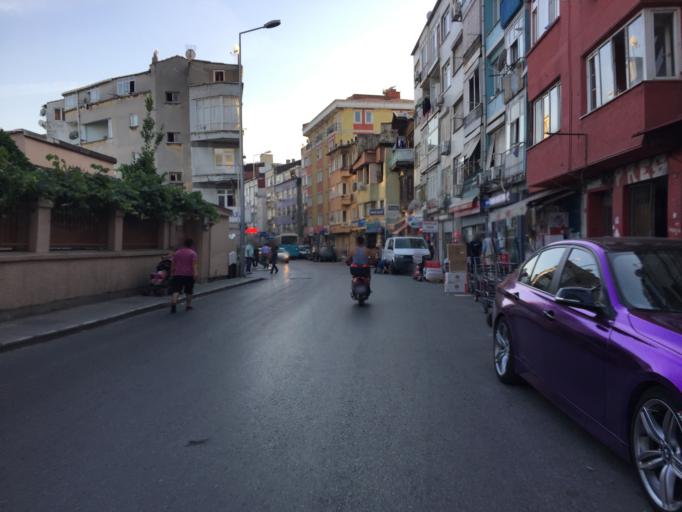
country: TR
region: Istanbul
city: Istanbul
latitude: 41.0065
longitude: 28.9462
